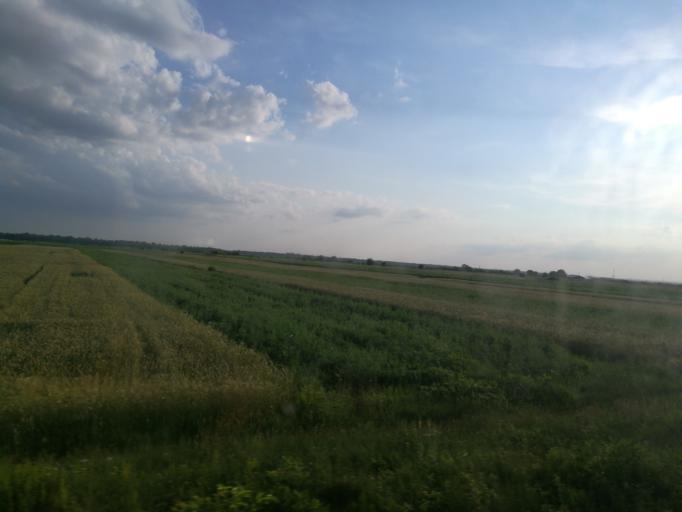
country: RO
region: Arges
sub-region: Comuna Leordeni
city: Leordeni
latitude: 44.7959
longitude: 25.1005
